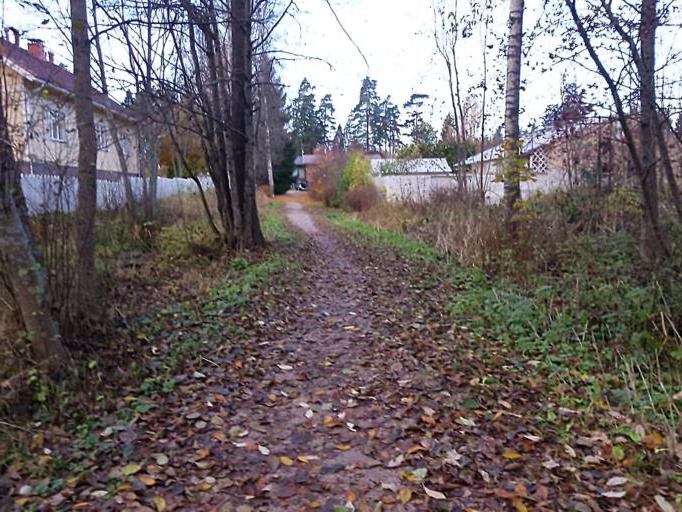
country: FI
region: Uusimaa
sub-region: Helsinki
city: Teekkarikylae
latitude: 60.2553
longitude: 24.8895
